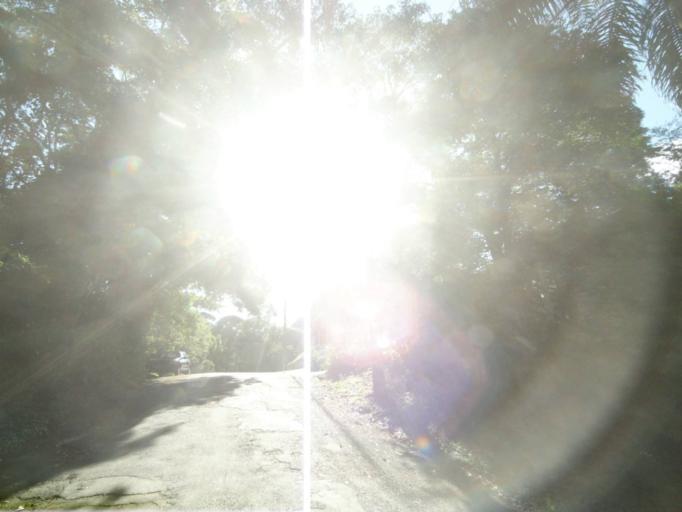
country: BR
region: Parana
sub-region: Curitiba
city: Curitiba
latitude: -25.4422
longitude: -49.3183
